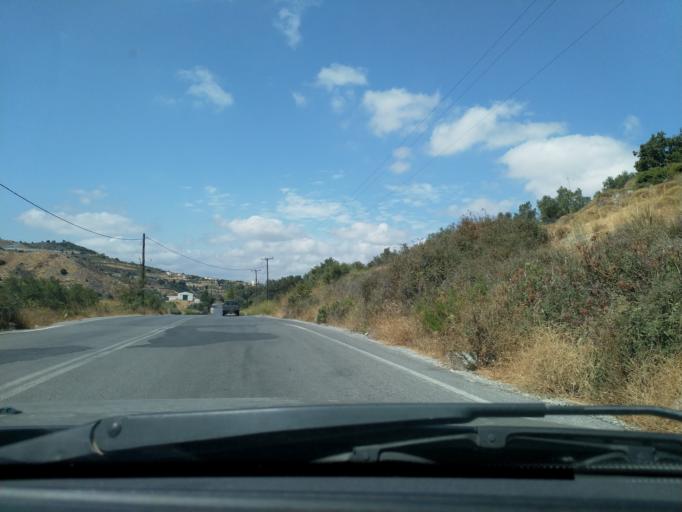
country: GR
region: Crete
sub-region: Nomos Rethymnis
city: Agia Foteini
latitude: 35.2074
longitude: 24.5397
